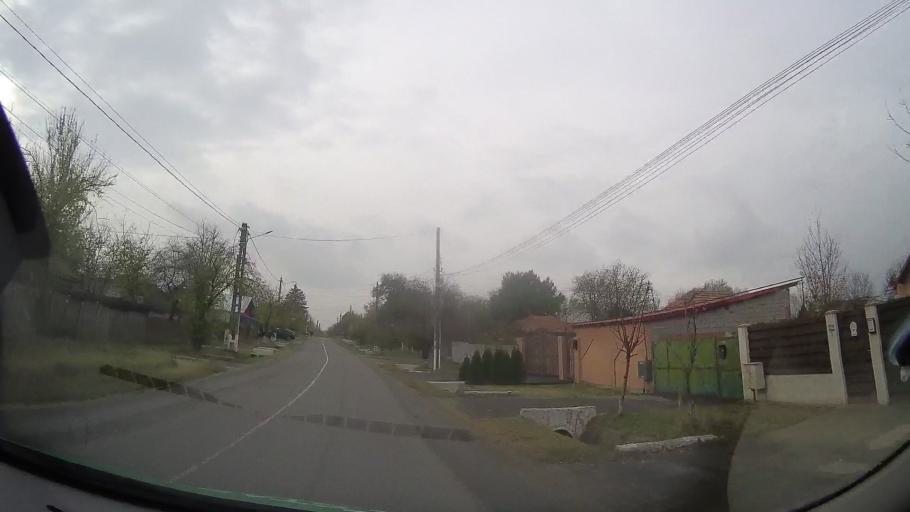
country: RO
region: Ilfov
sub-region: Comuna Gruiu
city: Gruiu
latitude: 44.7242
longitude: 26.2229
